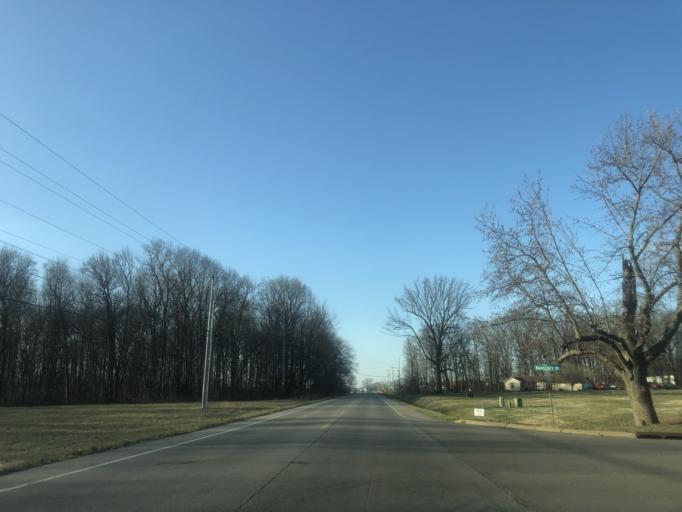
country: US
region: Tennessee
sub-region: Sumner County
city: Portland
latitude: 36.6259
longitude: -86.5576
